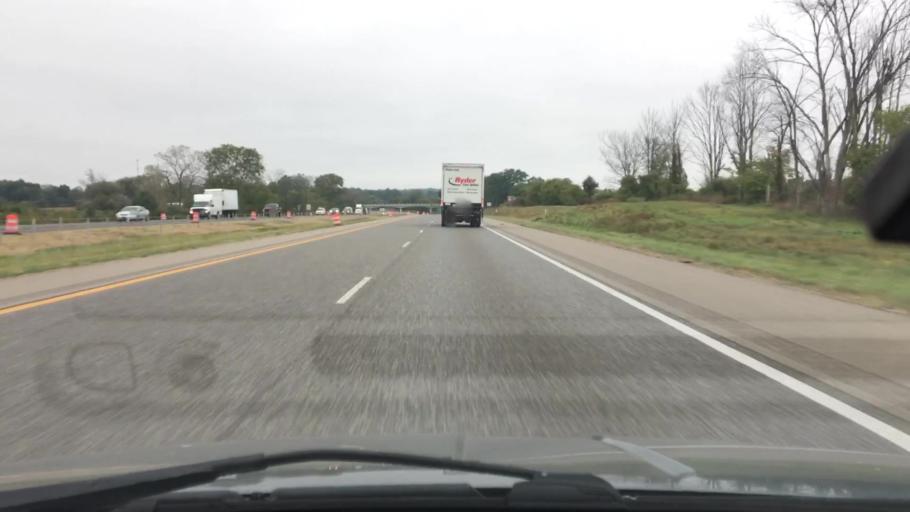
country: US
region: Michigan
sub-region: Van Buren County
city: Decatur
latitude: 42.1946
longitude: -86.0245
